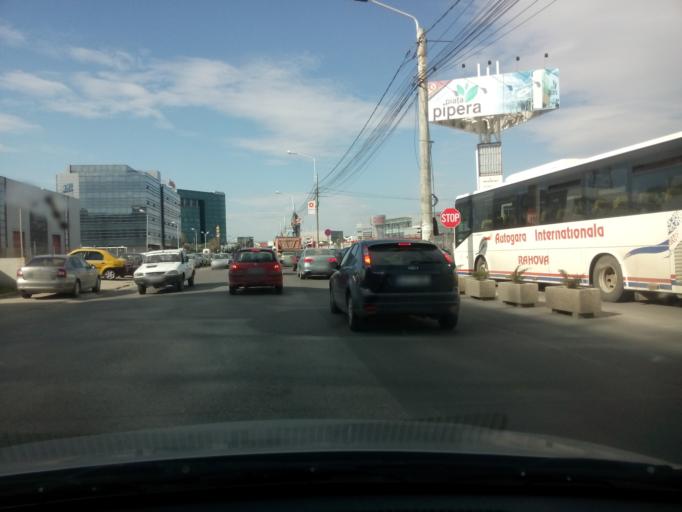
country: RO
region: Ilfov
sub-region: Voluntari City
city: Voluntari
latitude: 44.4895
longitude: 26.1264
